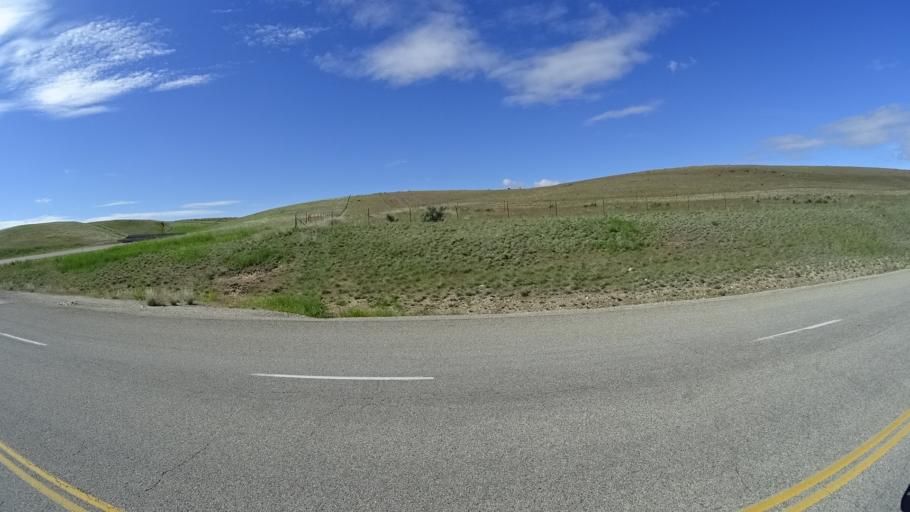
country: US
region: Idaho
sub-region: Ada County
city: Boise
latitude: 43.5078
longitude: -116.1461
